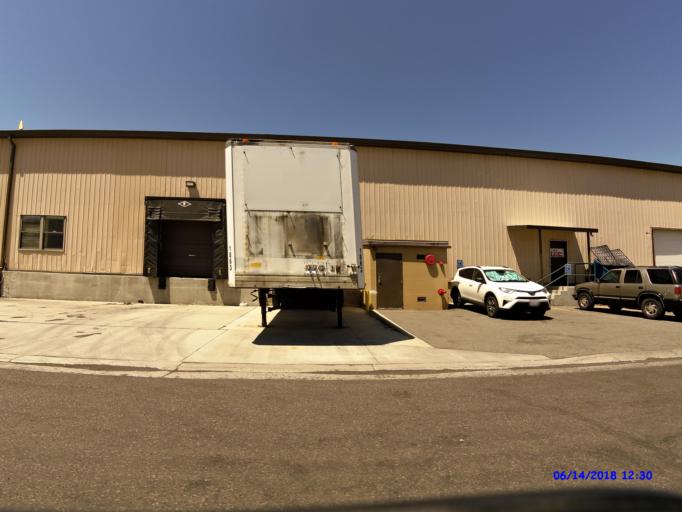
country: US
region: Utah
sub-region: Weber County
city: Harrisville
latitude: 41.2612
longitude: -112.0026
